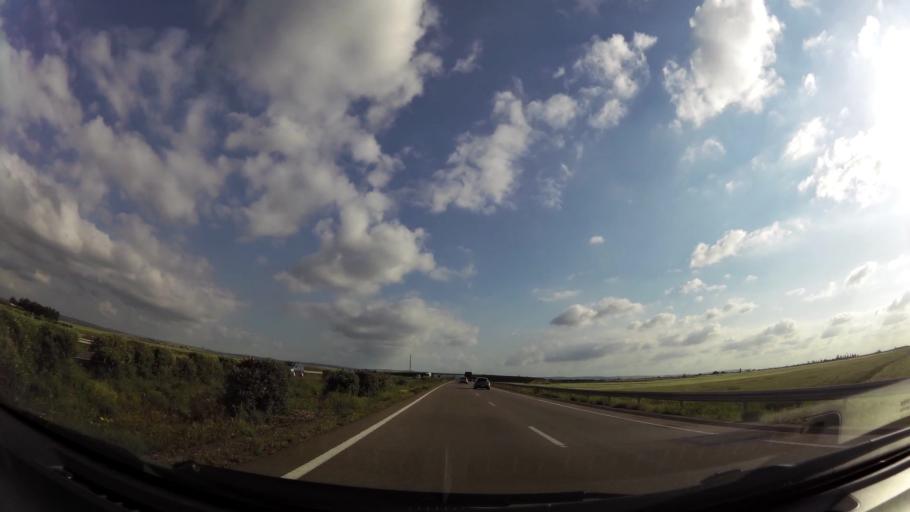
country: MA
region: Chaouia-Ouardigha
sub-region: Settat Province
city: Berrechid
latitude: 33.1517
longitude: -7.5721
